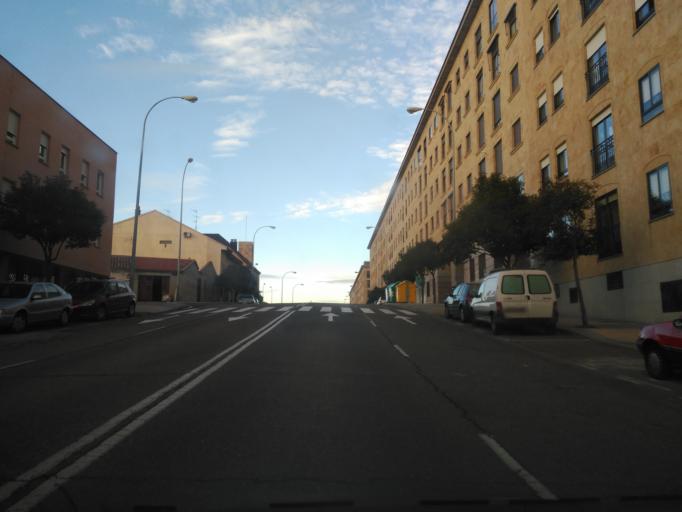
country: ES
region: Castille and Leon
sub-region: Provincia de Salamanca
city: Salamanca
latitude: 40.9796
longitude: -5.6680
